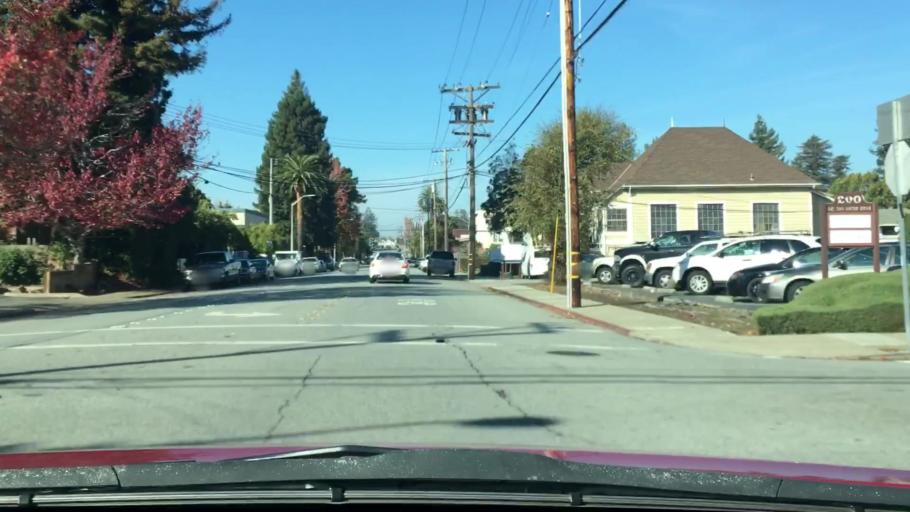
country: US
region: California
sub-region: San Mateo County
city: San Mateo
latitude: 37.5697
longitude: -122.3296
